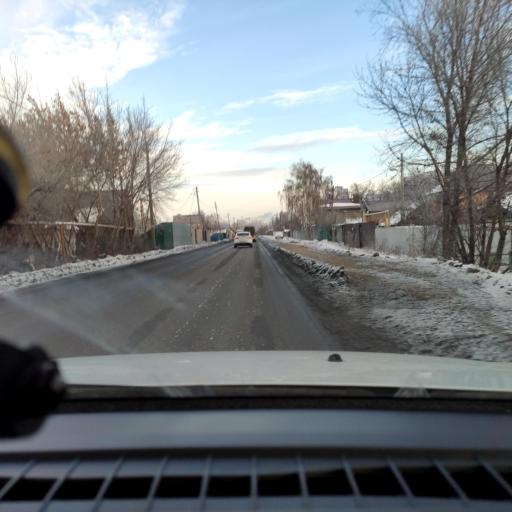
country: RU
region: Samara
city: Rozhdestveno
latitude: 53.1469
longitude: 50.0685
